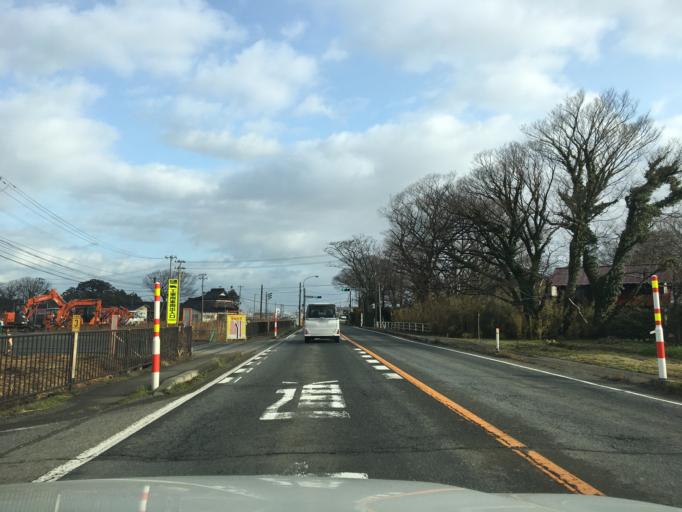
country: JP
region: Yamagata
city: Sakata
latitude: 38.8436
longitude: 139.8488
